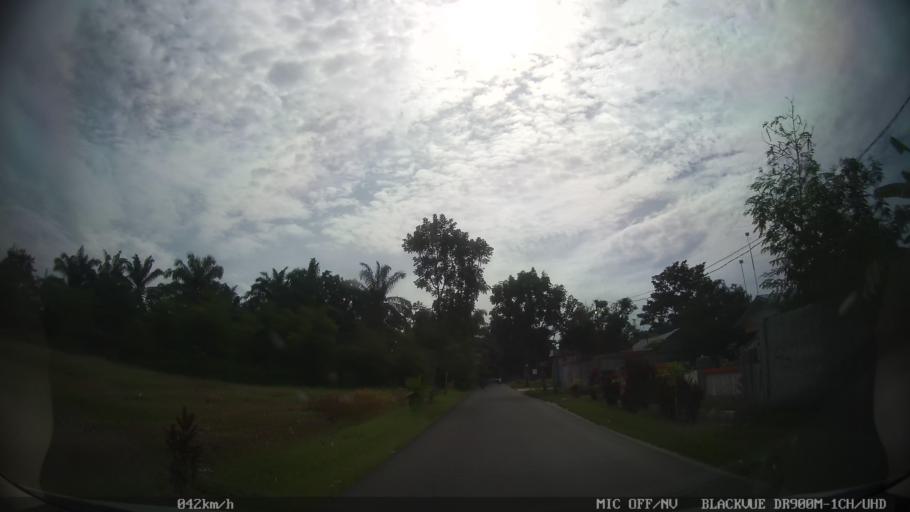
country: ID
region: North Sumatra
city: Percut
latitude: 3.6200
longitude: 98.7893
